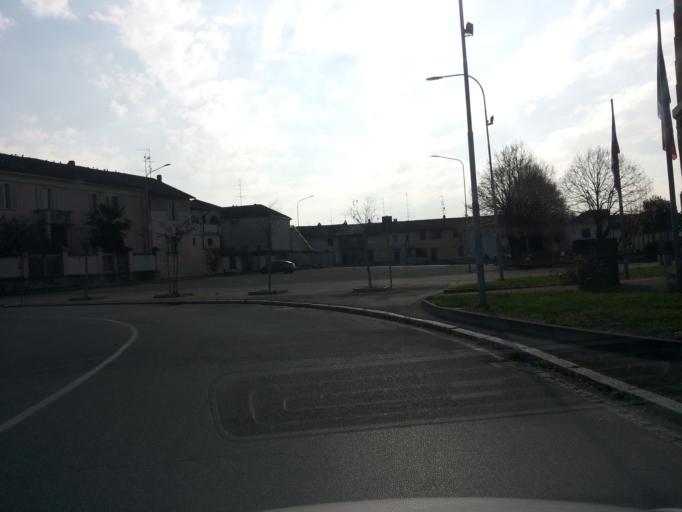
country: IT
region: Piedmont
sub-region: Provincia di Vercelli
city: Caresana
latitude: 45.2217
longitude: 8.5029
